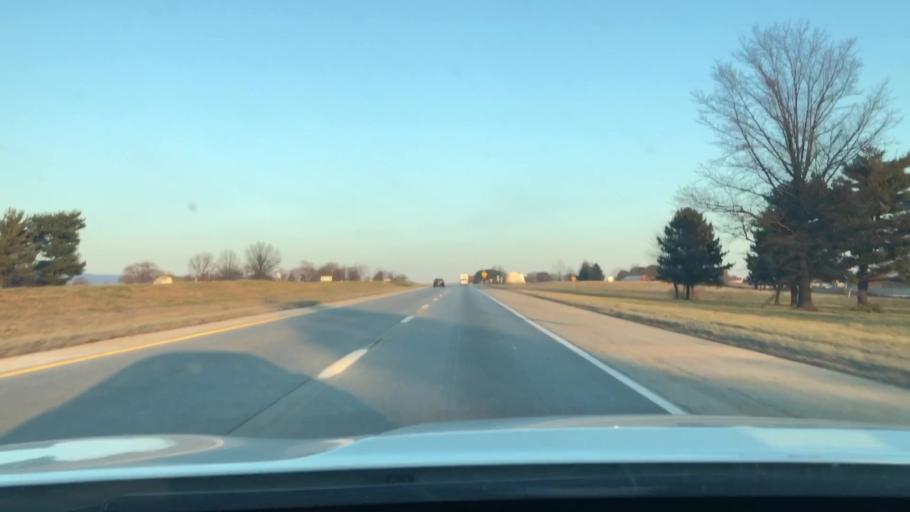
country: US
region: Pennsylvania
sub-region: Lebanon County
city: Fredericksburg
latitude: 40.4541
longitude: -76.3865
